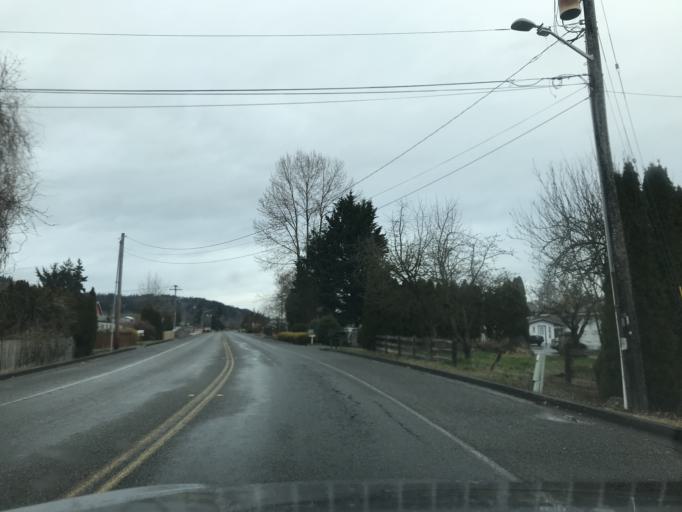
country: US
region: Washington
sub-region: King County
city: Algona
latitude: 47.2875
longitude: -122.2550
